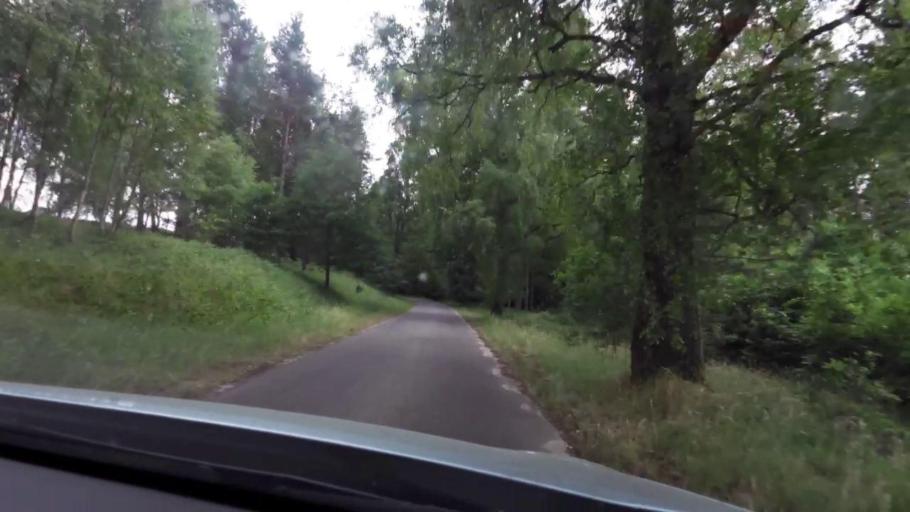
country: PL
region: Pomeranian Voivodeship
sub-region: Powiat bytowski
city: Trzebielino
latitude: 54.2546
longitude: 17.0048
